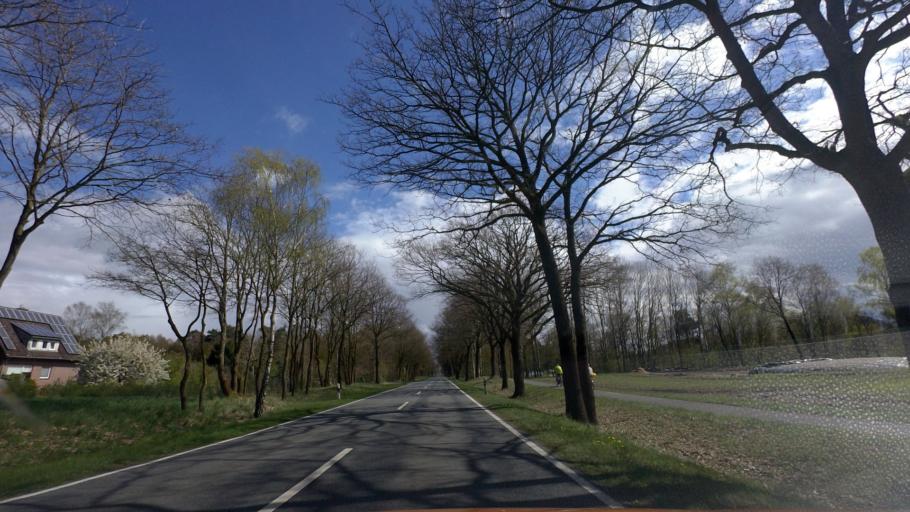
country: DE
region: Lower Saxony
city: Fintel
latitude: 53.1128
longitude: 9.7167
